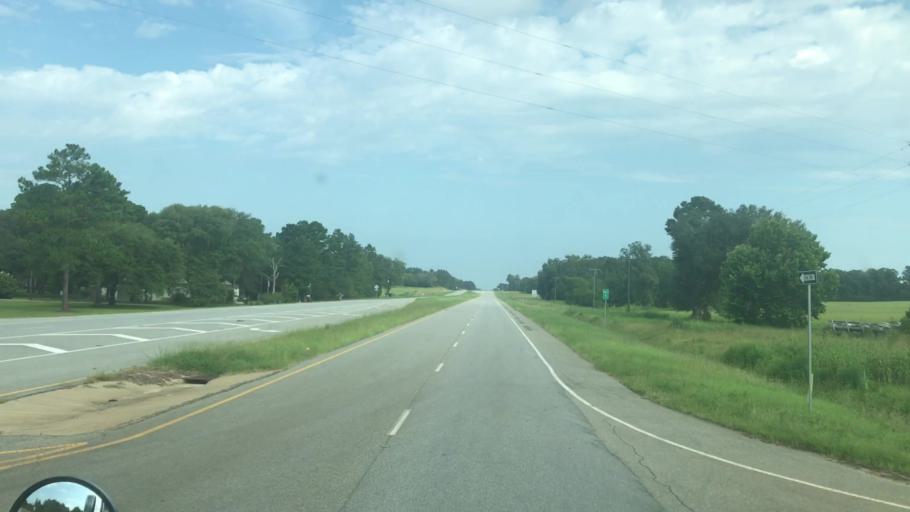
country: US
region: Georgia
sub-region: Early County
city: Blakely
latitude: 31.3038
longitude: -84.8635
